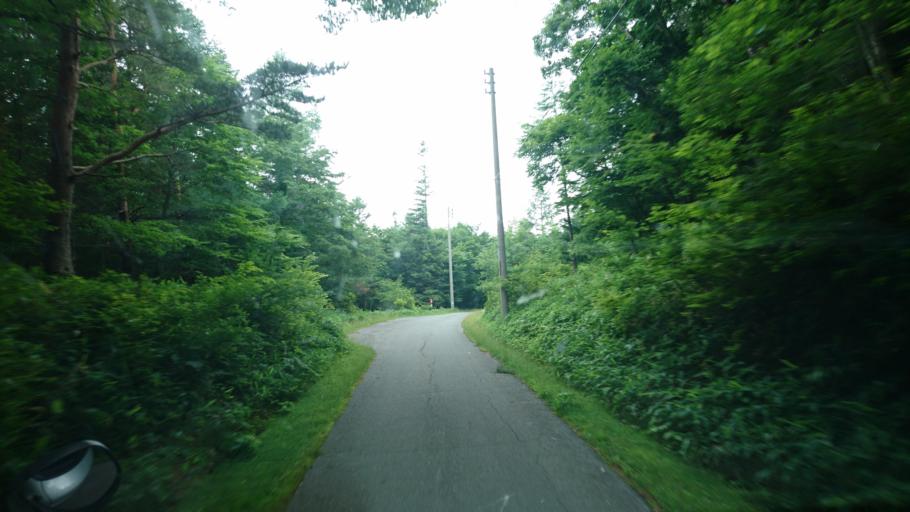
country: JP
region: Iwate
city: Ofunato
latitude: 39.1691
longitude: 141.7558
